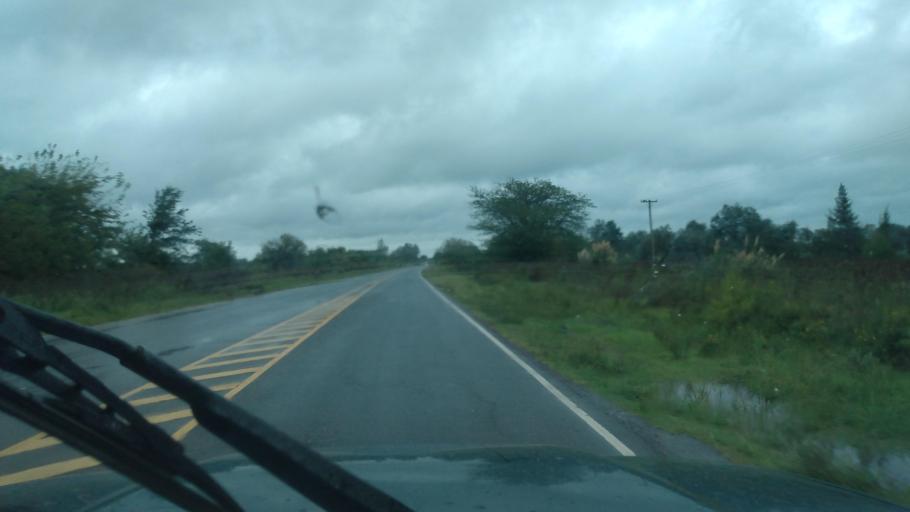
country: AR
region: Buenos Aires
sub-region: Partido de Lujan
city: Lujan
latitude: -34.4743
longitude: -59.0712
